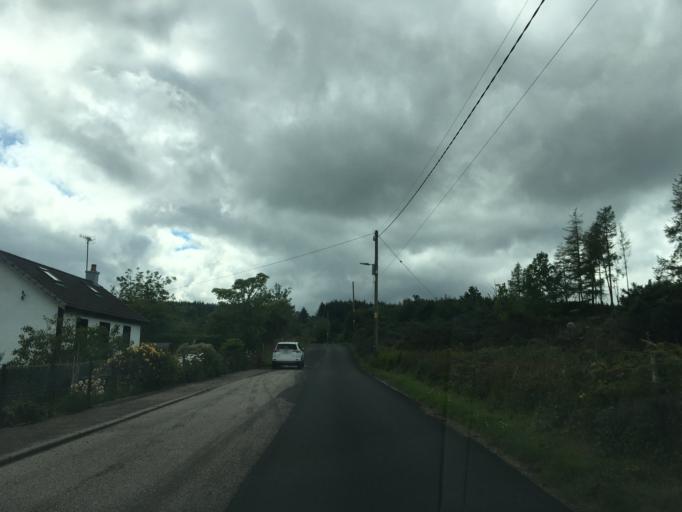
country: GB
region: Scotland
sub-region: Argyll and Bute
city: Tarbert
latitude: 55.8841
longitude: -5.2701
